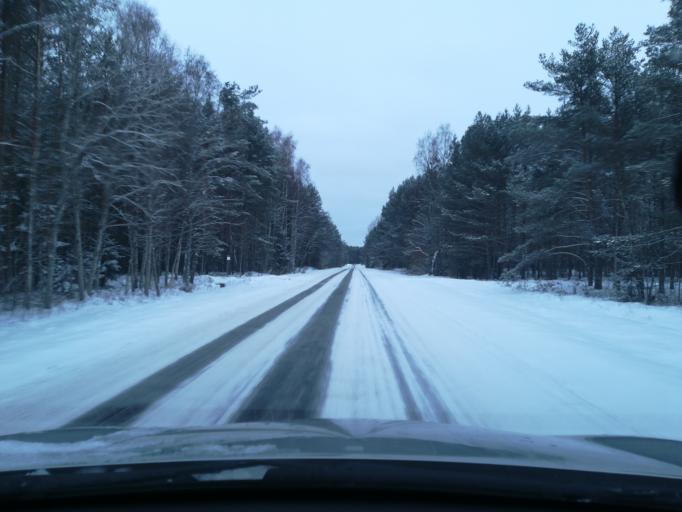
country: EE
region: Harju
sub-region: Keila linn
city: Keila
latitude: 59.3872
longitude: 24.2970
